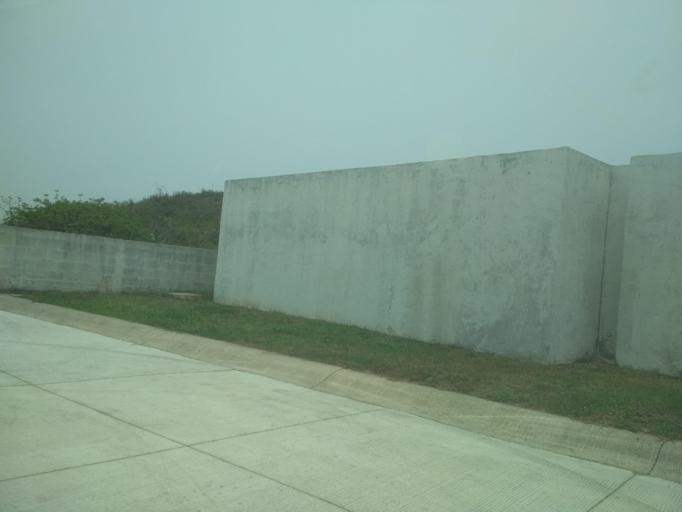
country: MX
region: Veracruz
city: Anton Lizardo
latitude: 19.0553
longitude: -96.0466
